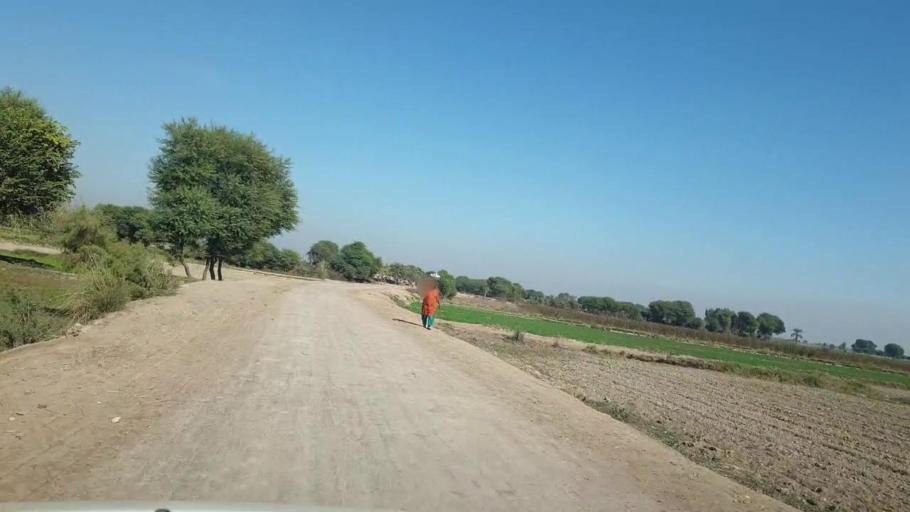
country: PK
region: Sindh
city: Dadu
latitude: 26.7948
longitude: 67.8294
